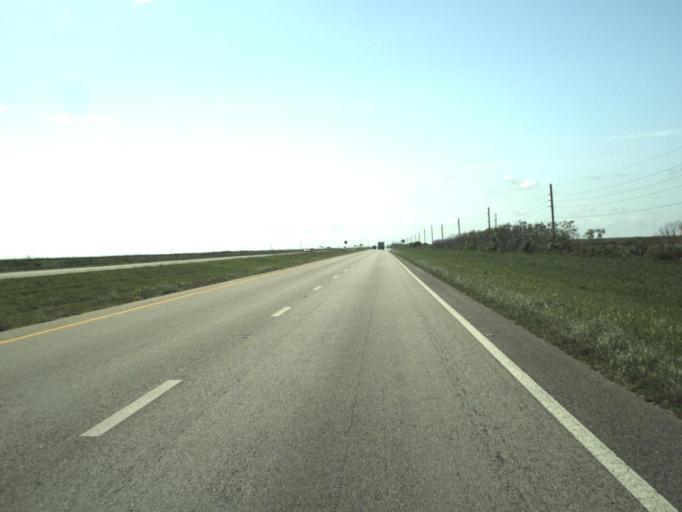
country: US
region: Florida
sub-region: Palm Beach County
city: Belle Glade Camp
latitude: 26.4188
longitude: -80.6029
